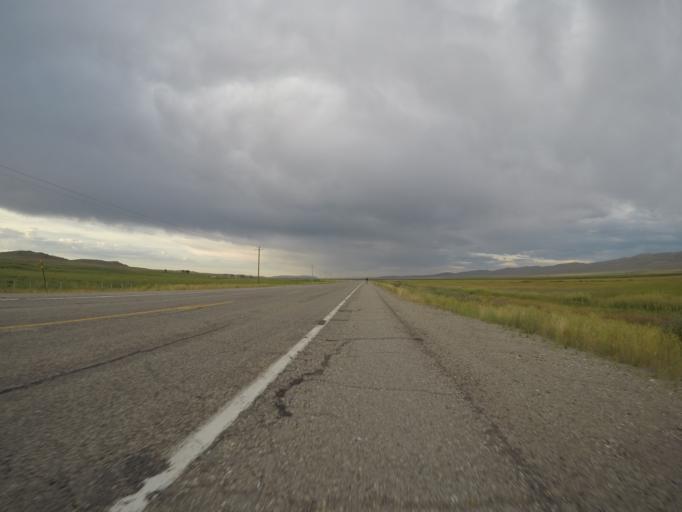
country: US
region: Utah
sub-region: Rich County
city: Randolph
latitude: 42.0188
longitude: -110.9348
